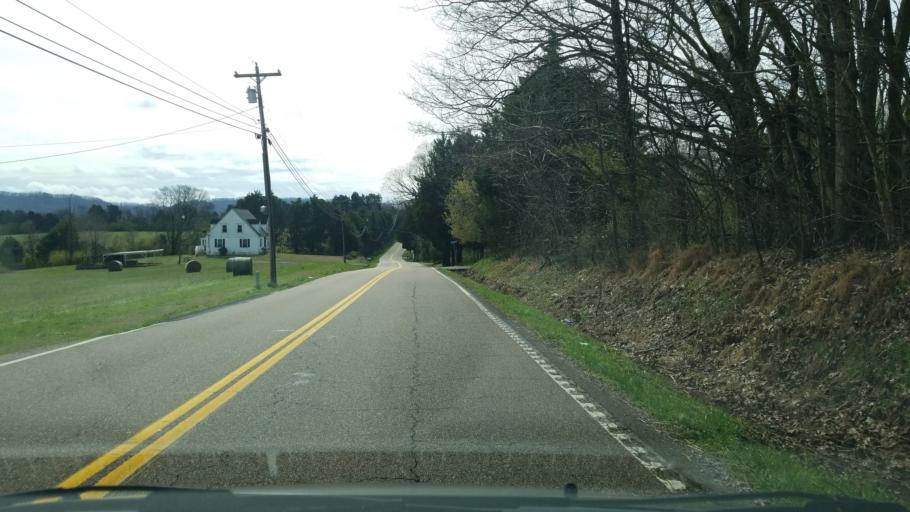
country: US
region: Tennessee
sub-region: Hamilton County
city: Collegedale
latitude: 35.1122
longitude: -85.0666
